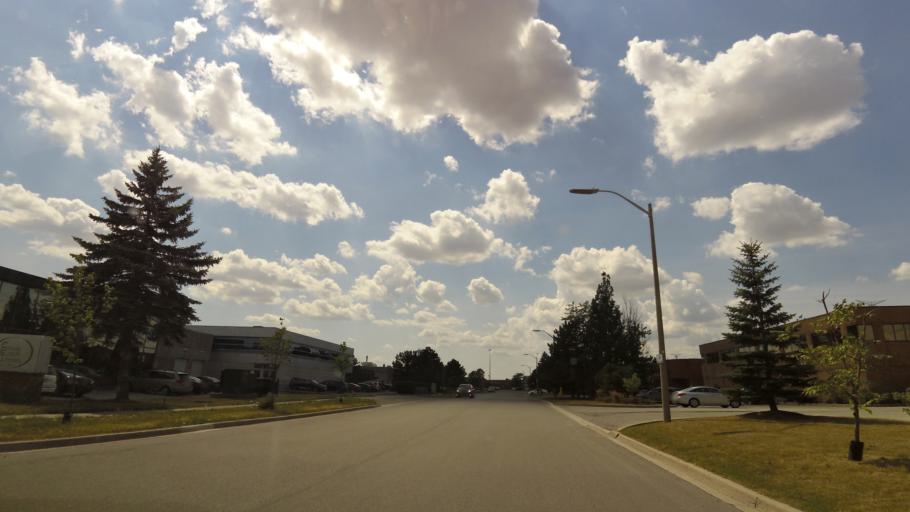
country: CA
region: Ontario
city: Concord
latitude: 43.7768
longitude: -79.5294
